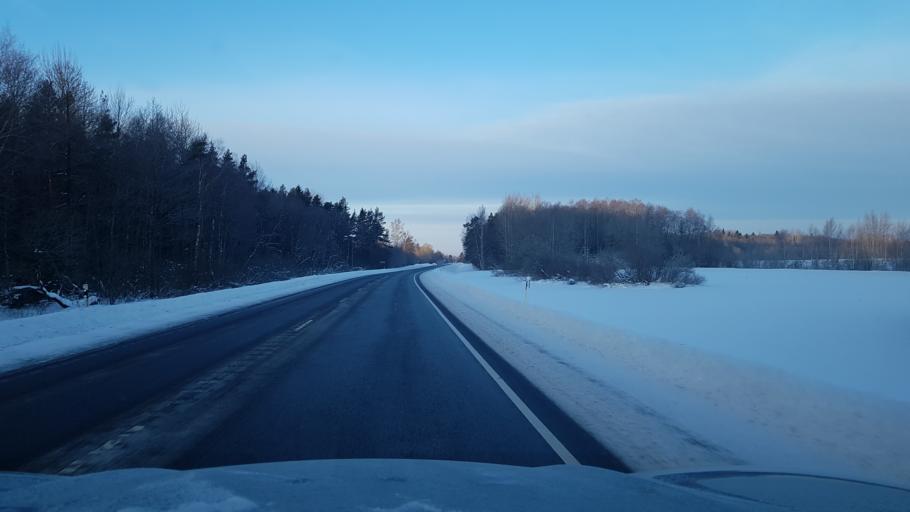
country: EE
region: Ida-Virumaa
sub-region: Toila vald
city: Voka
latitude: 59.3926
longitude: 27.6559
